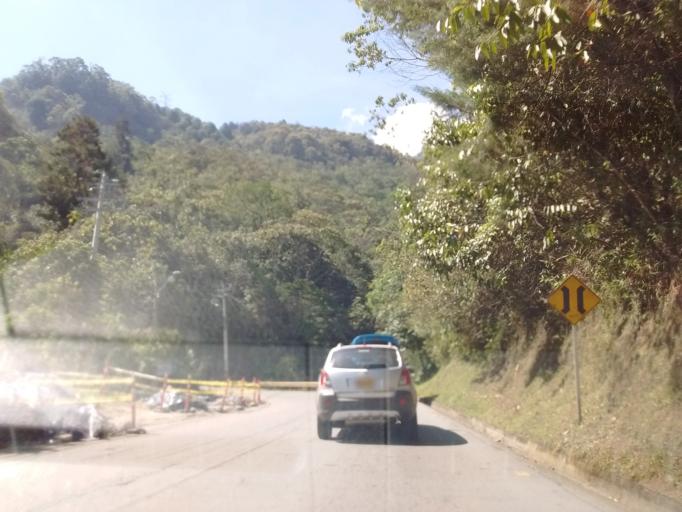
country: CO
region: Antioquia
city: Medellin
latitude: 6.2268
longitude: -75.5237
